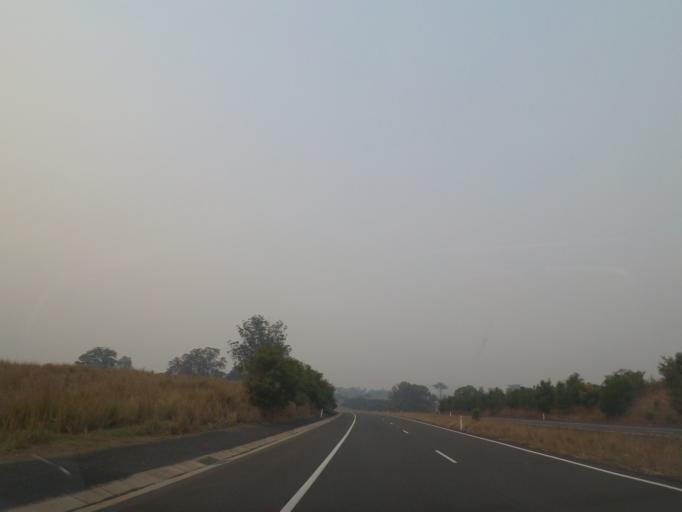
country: AU
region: New South Wales
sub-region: Nambucca Shire
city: Macksville
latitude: -30.7695
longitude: 152.9017
